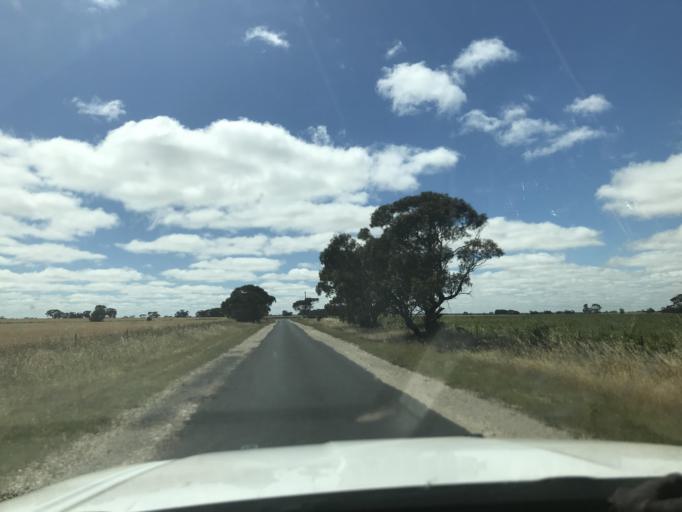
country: AU
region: South Australia
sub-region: Tatiara
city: Bordertown
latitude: -36.2815
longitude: 141.1457
